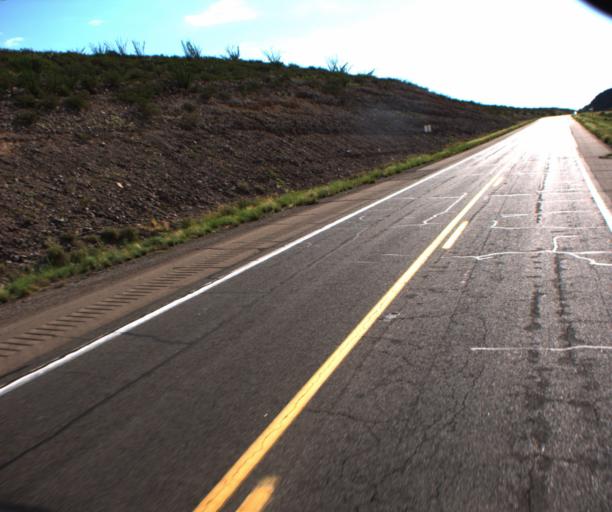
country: US
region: Arizona
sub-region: Greenlee County
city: Clifton
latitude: 32.8479
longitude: -109.4077
